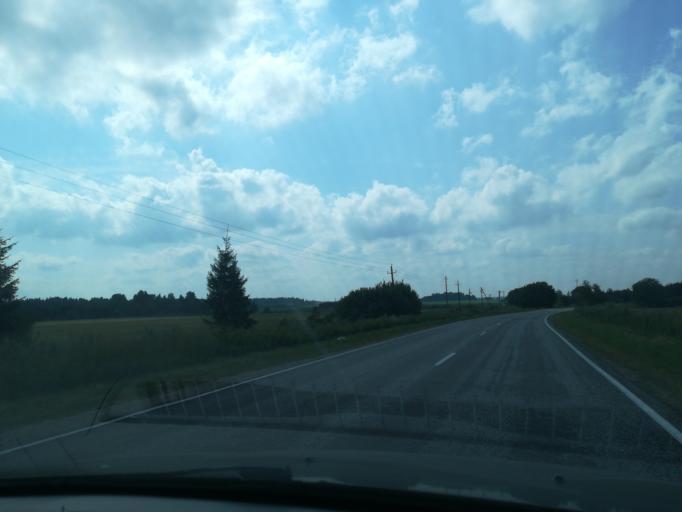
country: RU
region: Leningrad
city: Kopor'ye
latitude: 59.7101
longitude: 29.0871
